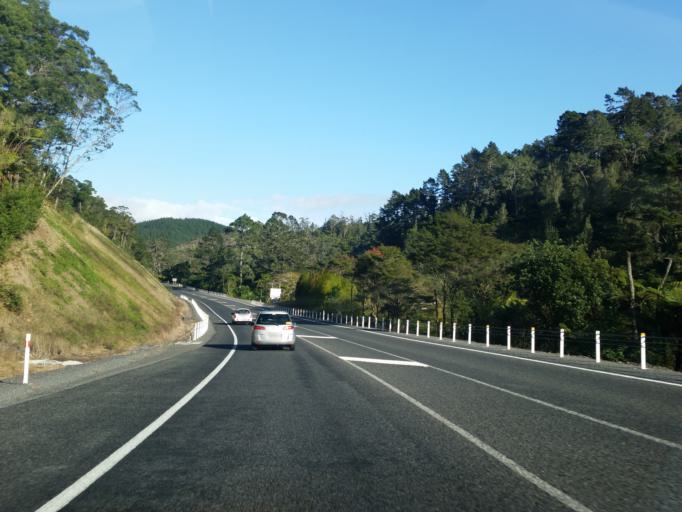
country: NZ
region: Bay of Plenty
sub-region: Western Bay of Plenty District
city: Waihi Beach
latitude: -37.4583
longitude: 175.9238
